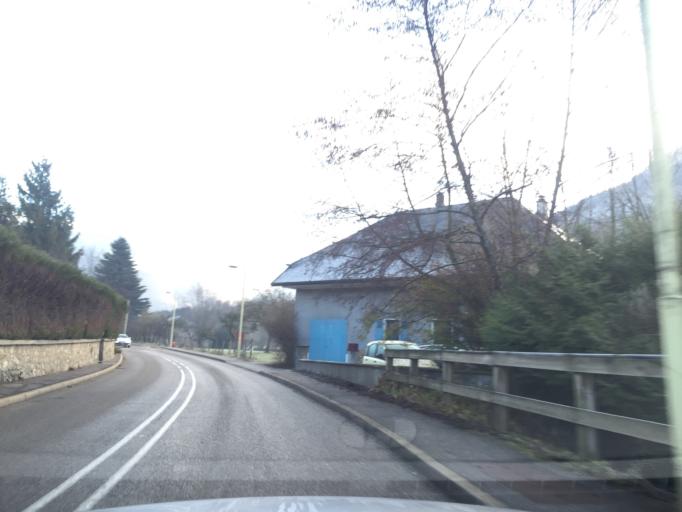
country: FR
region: Rhone-Alpes
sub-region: Departement de la Haute-Savoie
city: Cusy
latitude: 45.7620
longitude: 6.0246
